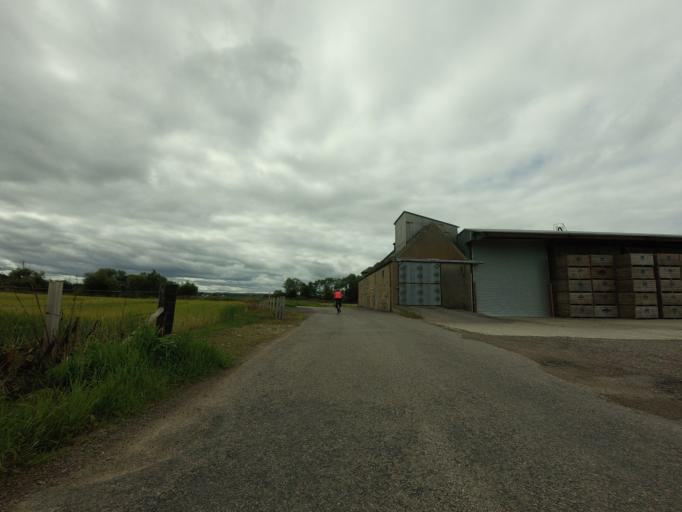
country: GB
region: Scotland
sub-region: Moray
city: Forres
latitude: 57.6258
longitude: -3.6064
